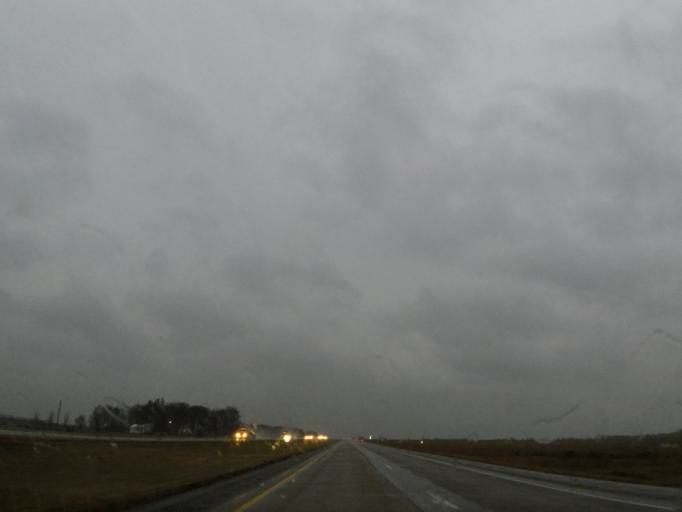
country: US
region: Iowa
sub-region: Cerro Gordo County
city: Clear Lake
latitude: 43.2276
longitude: -93.3486
